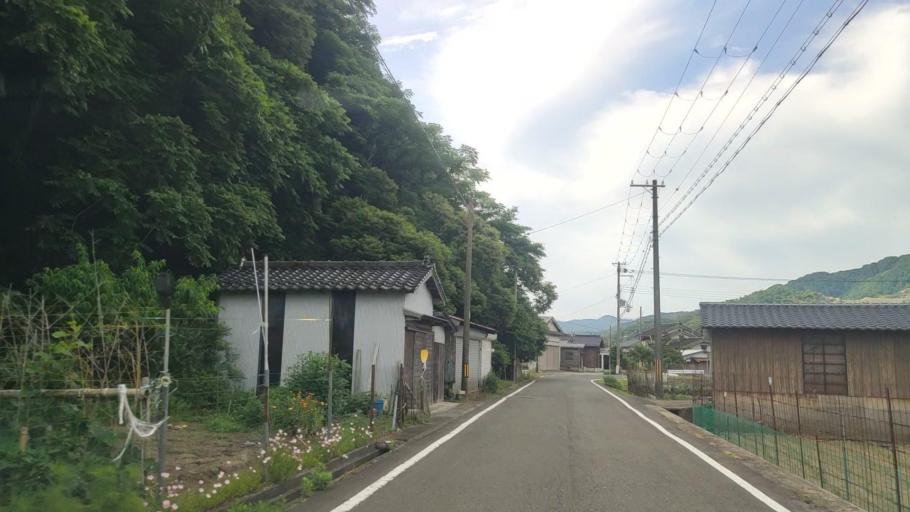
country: JP
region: Hyogo
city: Toyooka
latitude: 35.6393
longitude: 134.8402
